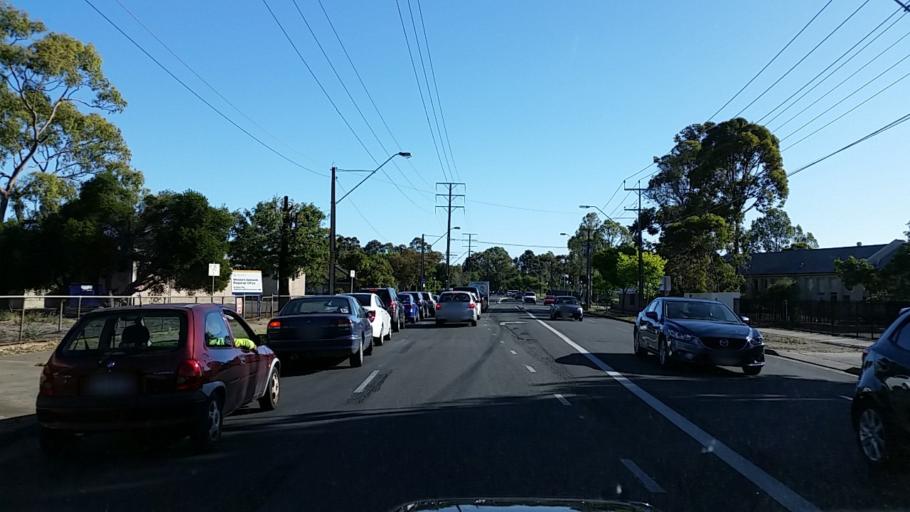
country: AU
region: South Australia
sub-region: Charles Sturt
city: Allenby Gardens
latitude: -34.9108
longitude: 138.5490
